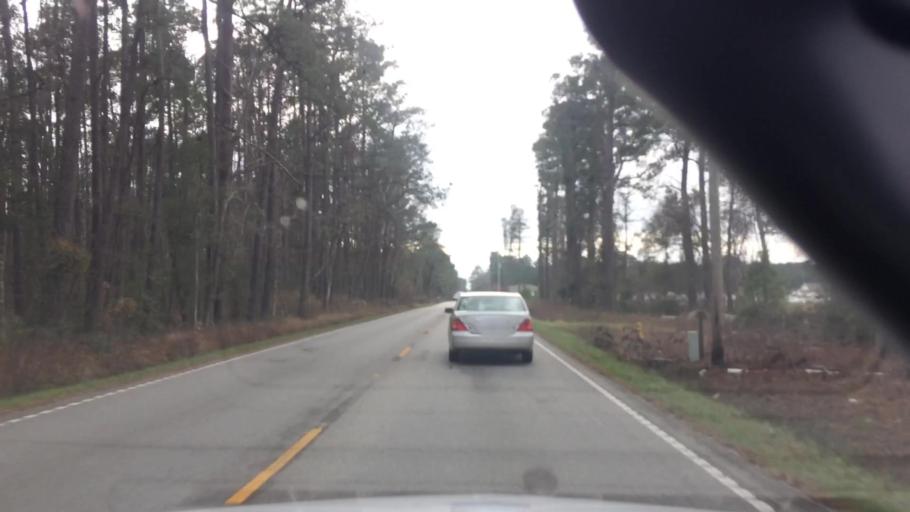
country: US
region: South Carolina
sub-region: Horry County
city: Little River
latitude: 33.8978
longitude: -78.6695
